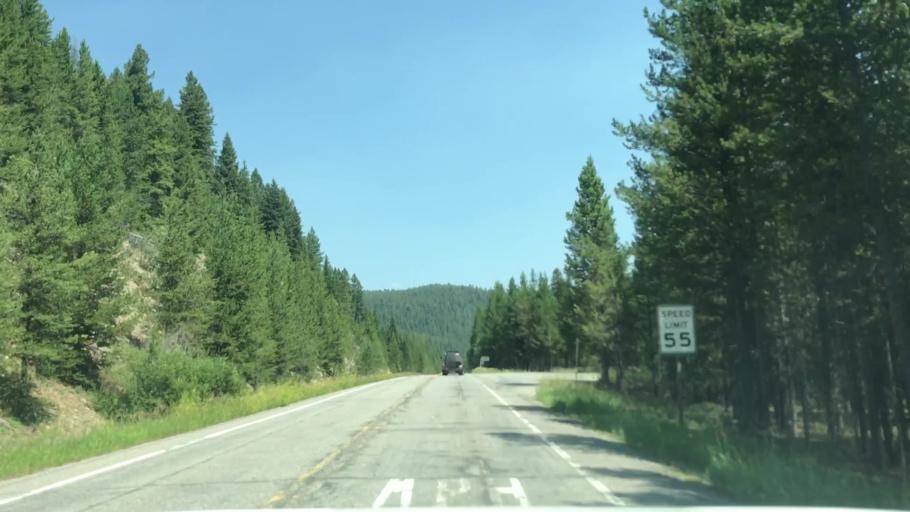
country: US
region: Montana
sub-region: Gallatin County
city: West Yellowstone
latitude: 44.8137
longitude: -111.0933
